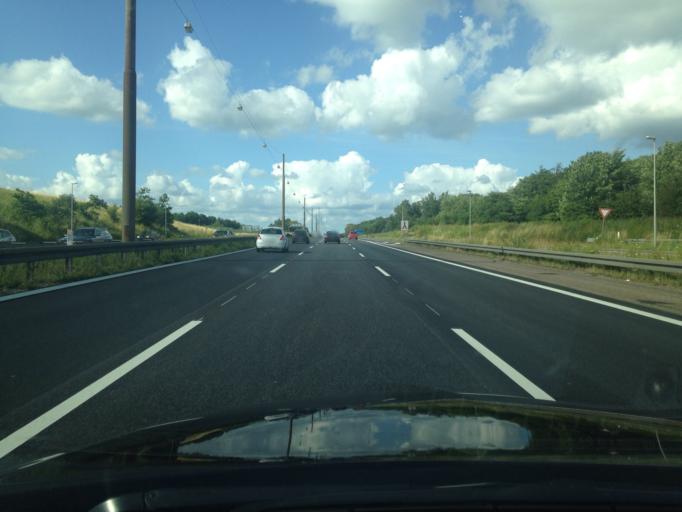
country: DK
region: Capital Region
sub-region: Lyngby-Tarbaek Kommune
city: Kongens Lyngby
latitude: 55.7765
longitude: 12.5250
